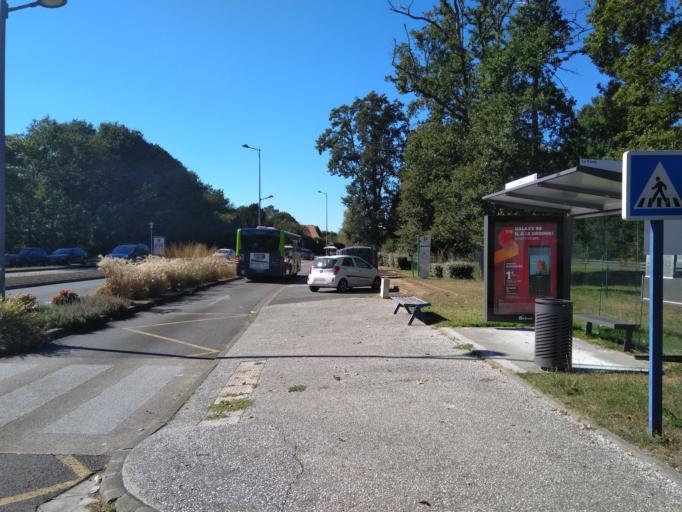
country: FR
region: Aquitaine
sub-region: Departement des Landes
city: Narrosse
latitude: 43.6940
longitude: -1.0126
